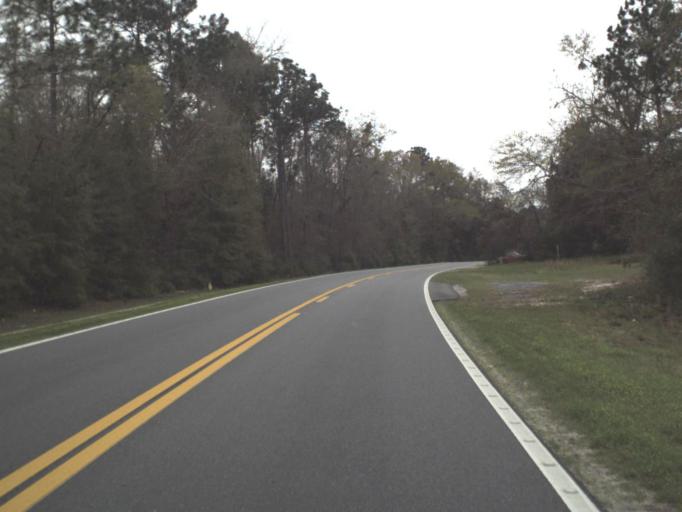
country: US
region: Florida
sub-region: Gulf County
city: Wewahitchka
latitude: 30.0239
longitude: -84.9803
